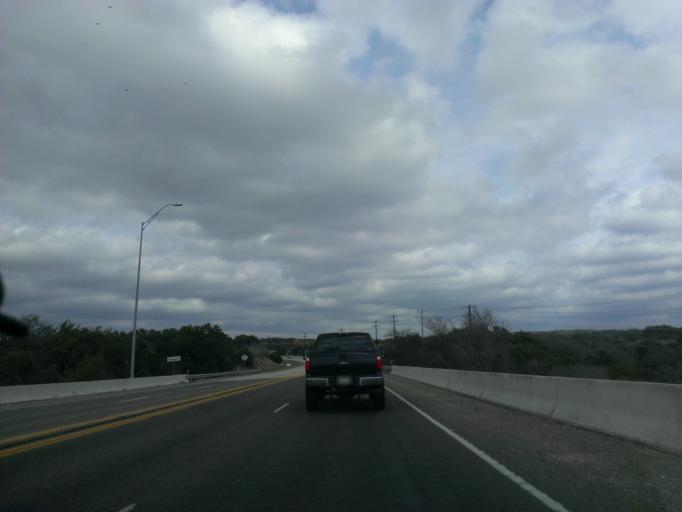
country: US
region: Texas
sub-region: Travis County
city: Briarcliff
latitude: 30.3902
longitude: -98.0863
